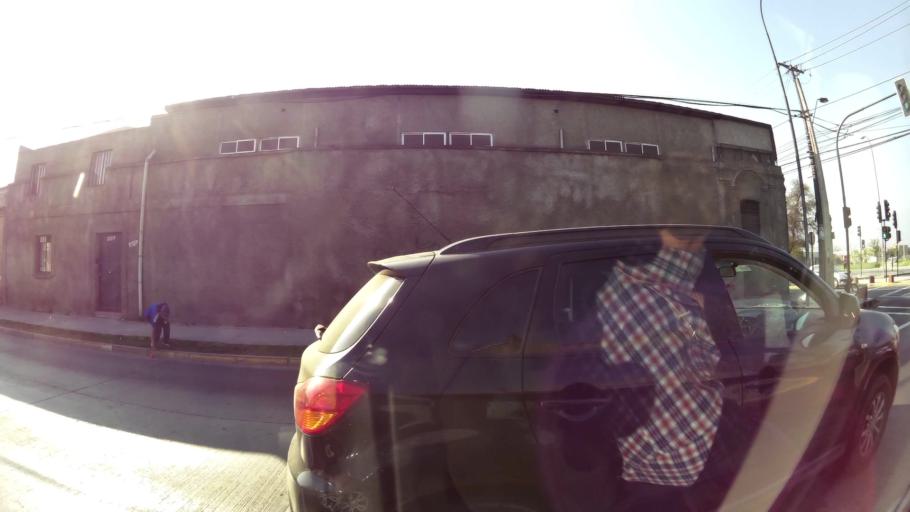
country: CL
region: Santiago Metropolitan
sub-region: Provincia de Santiago
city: Santiago
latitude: -33.3998
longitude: -70.6723
